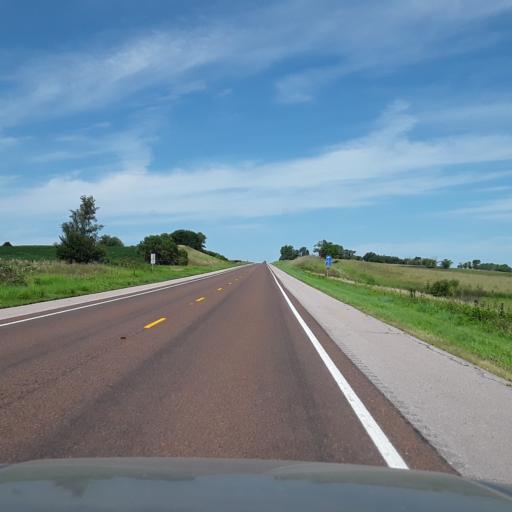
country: US
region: Nebraska
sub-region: Lancaster County
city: Lincoln
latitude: 40.8865
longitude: -96.8399
